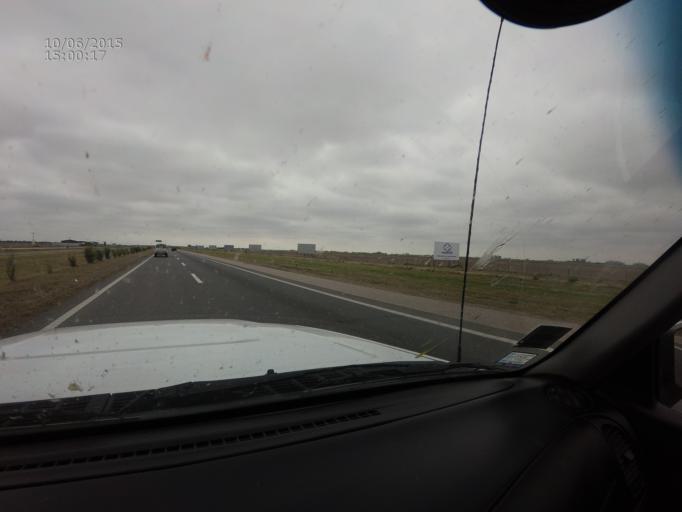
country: AR
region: Cordoba
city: Laguna Larga
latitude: -31.7682
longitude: -63.7599
